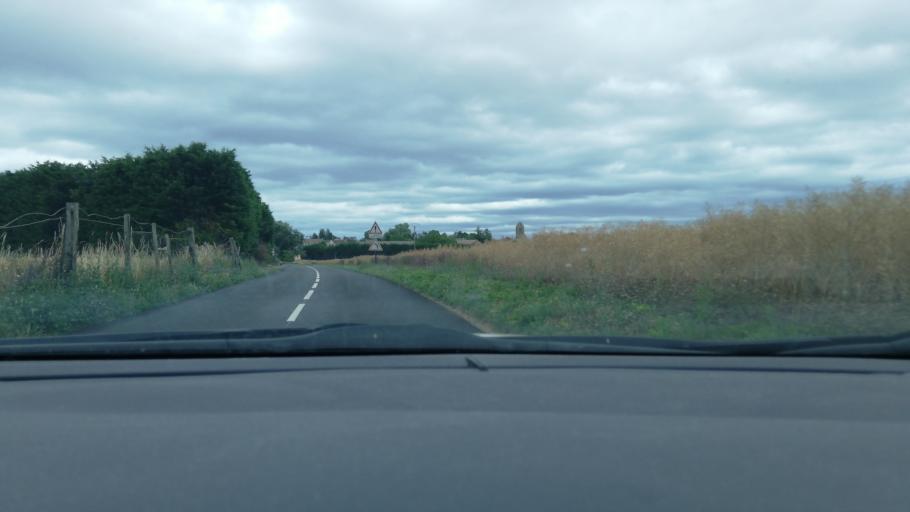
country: FR
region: Ile-de-France
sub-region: Departement du Val-d'Oise
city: Ennery
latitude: 49.1019
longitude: 2.1226
